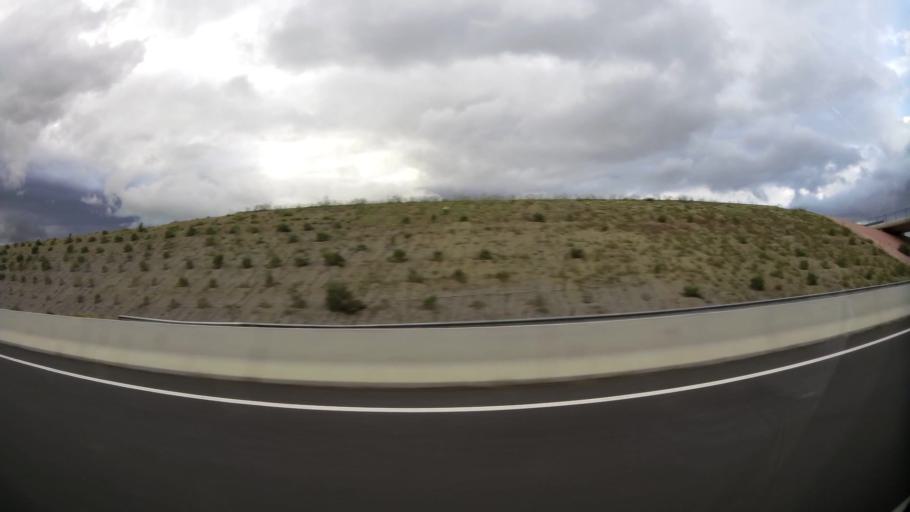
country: MA
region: Taza-Al Hoceima-Taounate
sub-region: Taza
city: Taza
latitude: 34.2530
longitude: -3.9255
